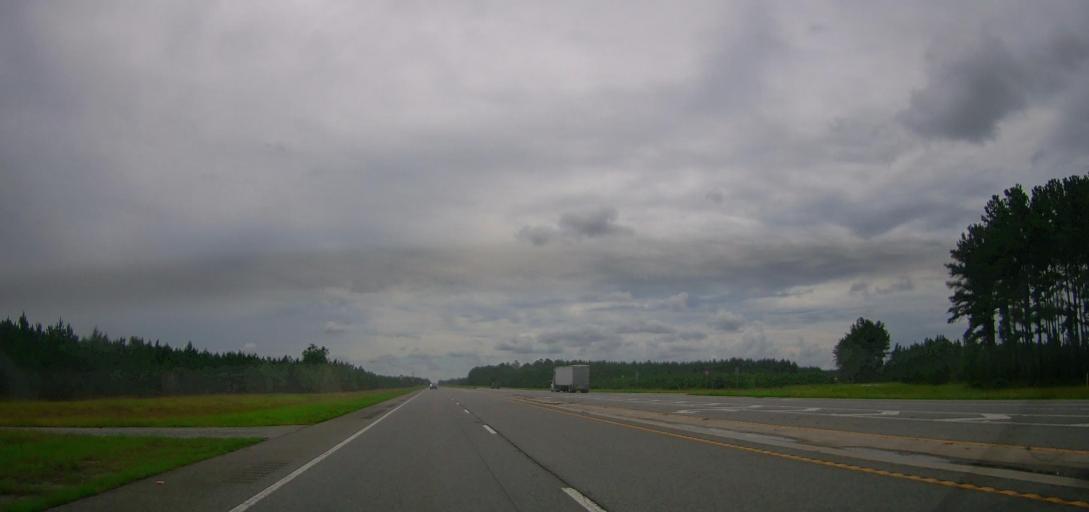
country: US
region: Georgia
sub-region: Appling County
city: Baxley
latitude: 31.7497
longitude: -82.2657
